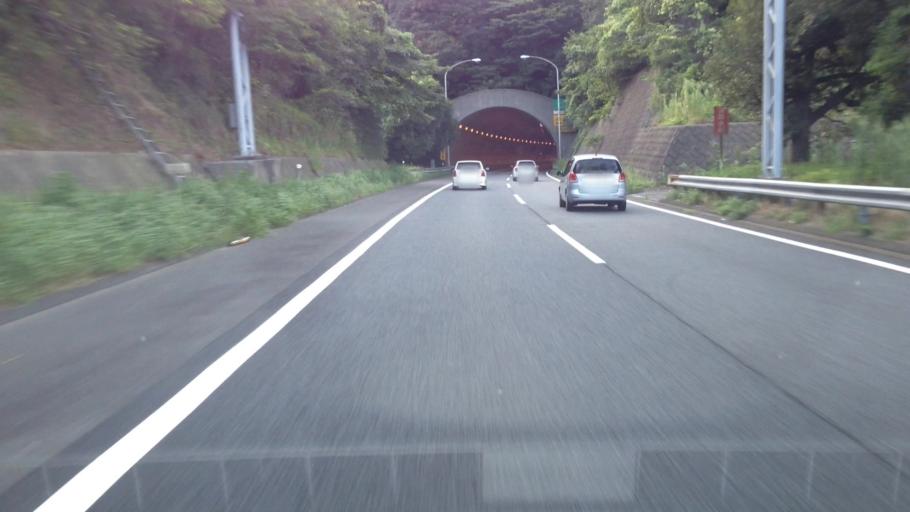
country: JP
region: Kanagawa
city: Yokosuka
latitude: 35.2841
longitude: 139.6243
